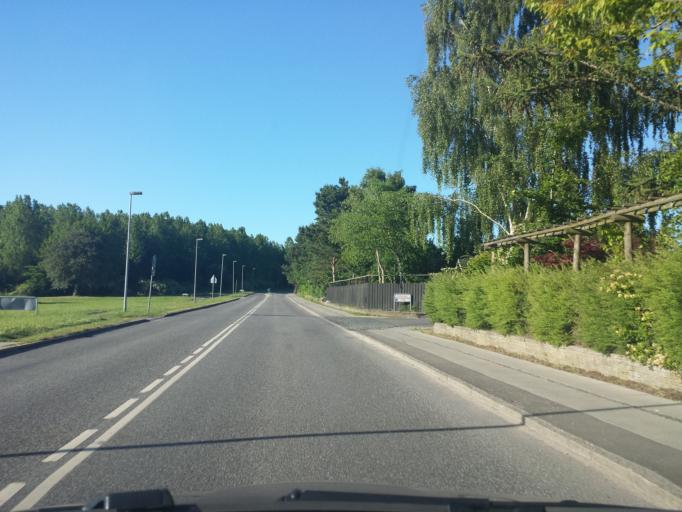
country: DK
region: Capital Region
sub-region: Ballerup Kommune
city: Ballerup
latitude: 55.7119
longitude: 12.3824
